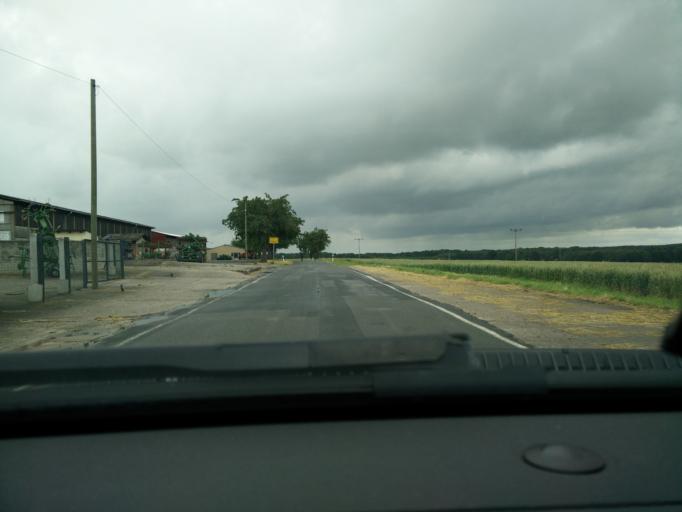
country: DE
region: Saxony
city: Bad Lausick
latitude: 51.1406
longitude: 12.6880
